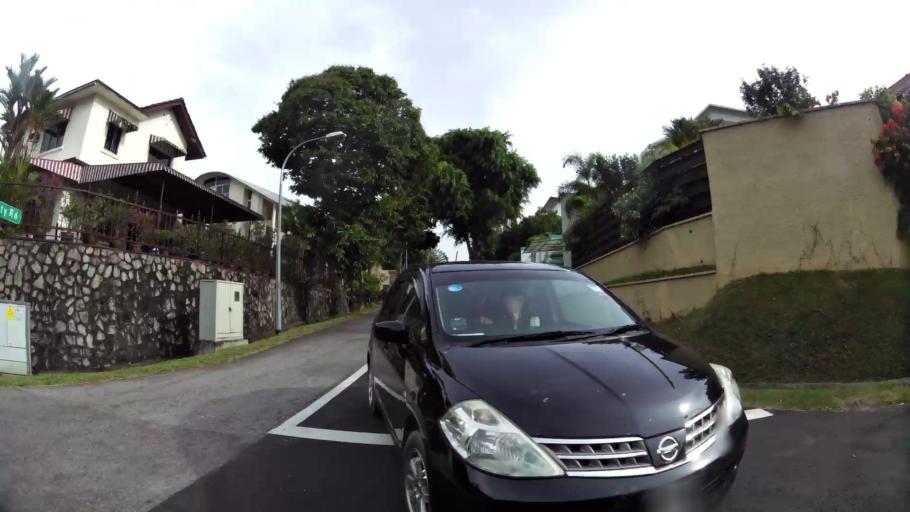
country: SG
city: Singapore
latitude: 1.3299
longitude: 103.8189
